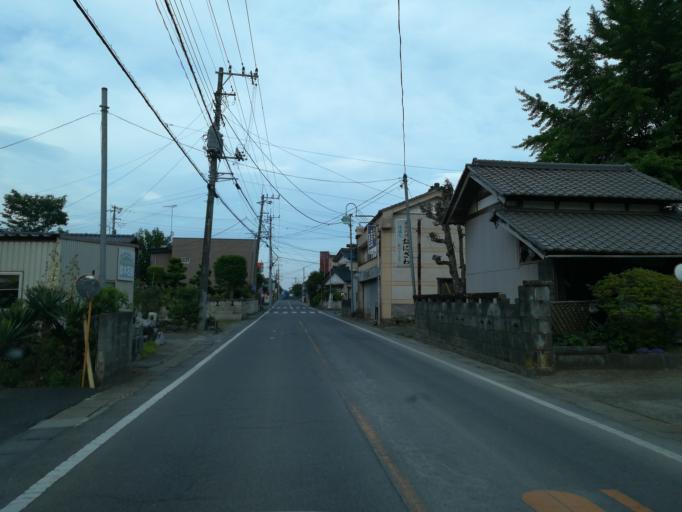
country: JP
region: Ibaraki
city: Tsukuba
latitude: 36.2228
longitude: 140.1602
